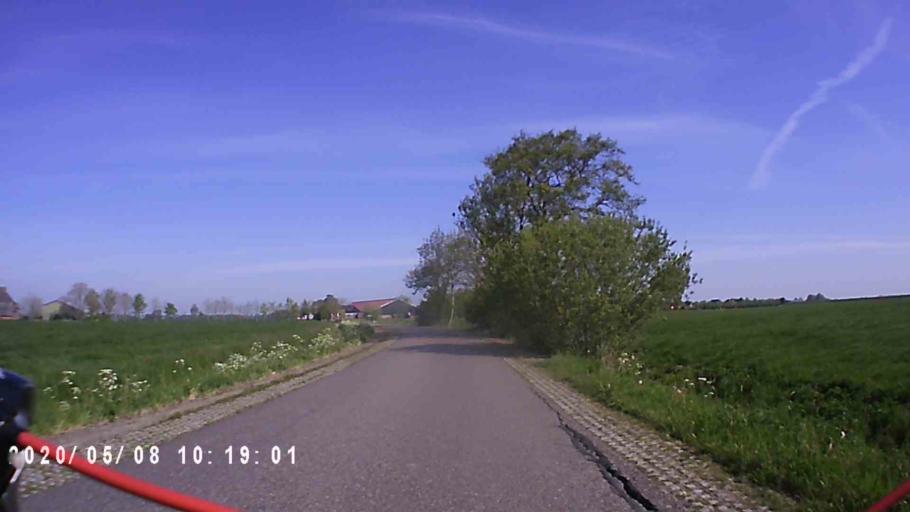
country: NL
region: Groningen
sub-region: Gemeente Winsum
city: Winsum
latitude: 53.2974
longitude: 6.4916
